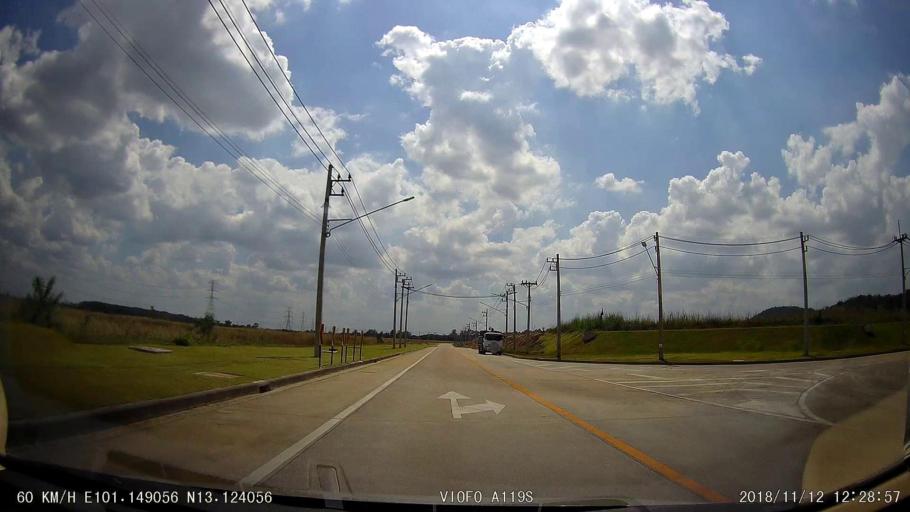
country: TH
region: Chon Buri
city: Ban Talat Bueng
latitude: 13.1236
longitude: 101.1490
